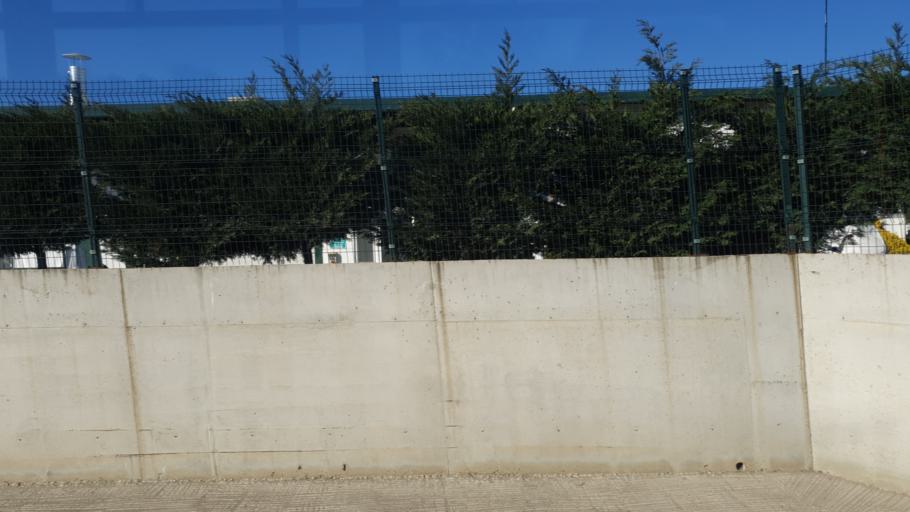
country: TR
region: Tekirdag
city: Velimese
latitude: 41.2558
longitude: 27.9117
